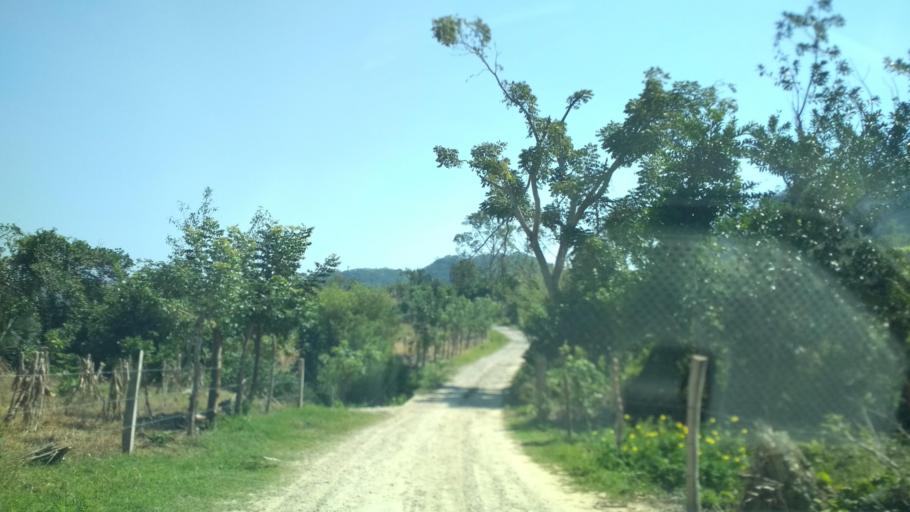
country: MX
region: Veracruz
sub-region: Papantla
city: Polutla
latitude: 20.4807
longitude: -97.2229
